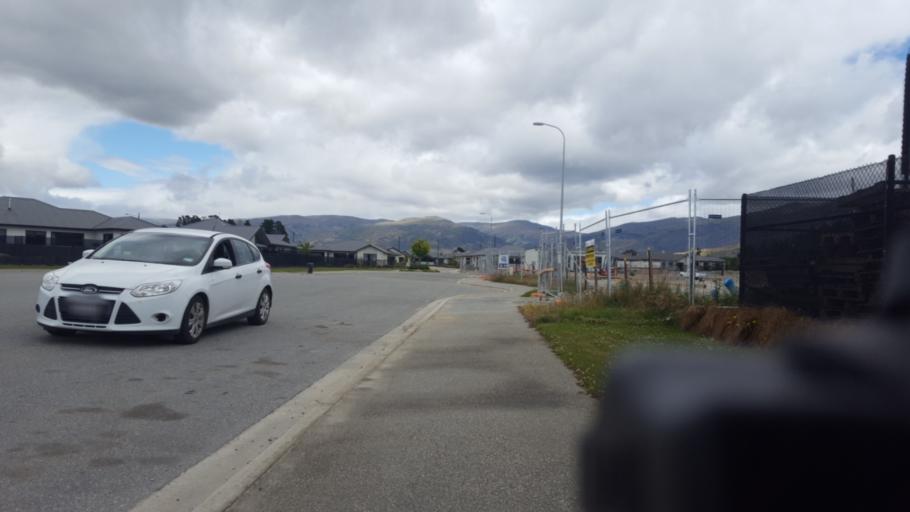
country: NZ
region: Otago
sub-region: Queenstown-Lakes District
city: Wanaka
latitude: -45.0352
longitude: 169.1919
